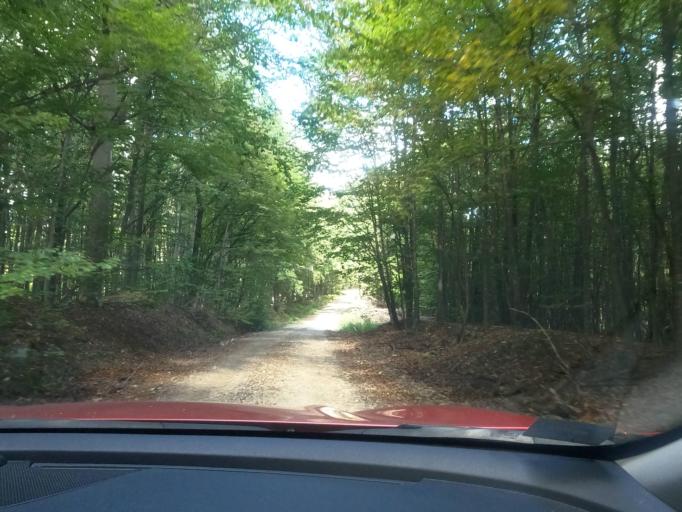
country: BA
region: Federation of Bosnia and Herzegovina
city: Velika Kladusa
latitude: 45.2693
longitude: 15.7777
